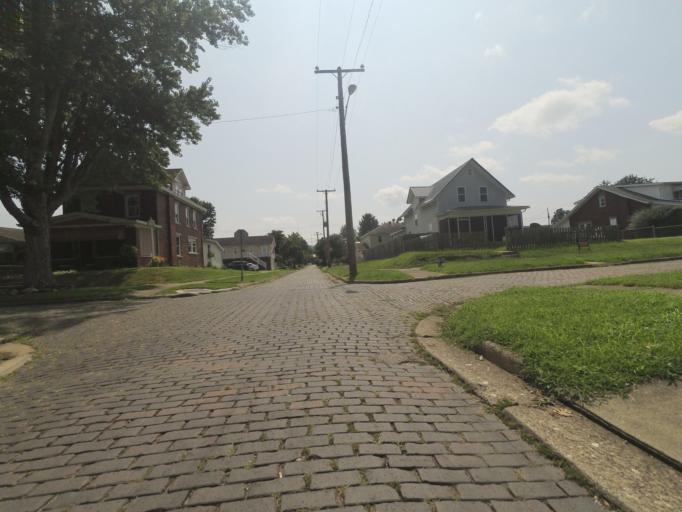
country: US
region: West Virginia
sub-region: Cabell County
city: Huntington
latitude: 38.4335
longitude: -82.4055
